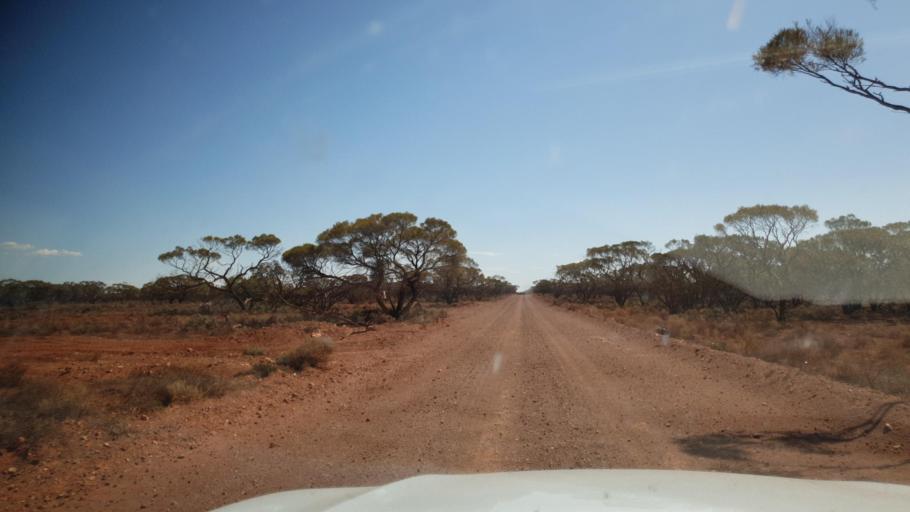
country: AU
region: South Australia
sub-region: Kimba
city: Caralue
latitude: -32.5255
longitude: 136.1630
